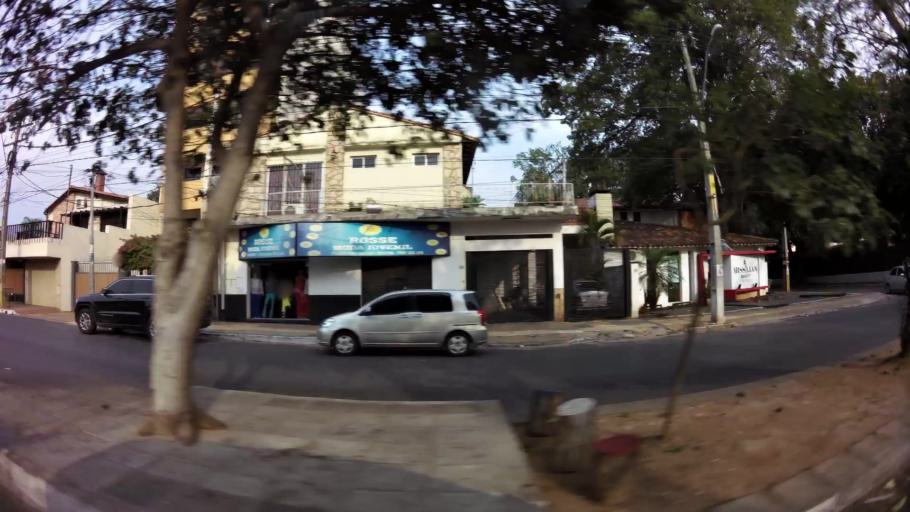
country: PY
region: Asuncion
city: Asuncion
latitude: -25.3063
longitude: -57.6083
